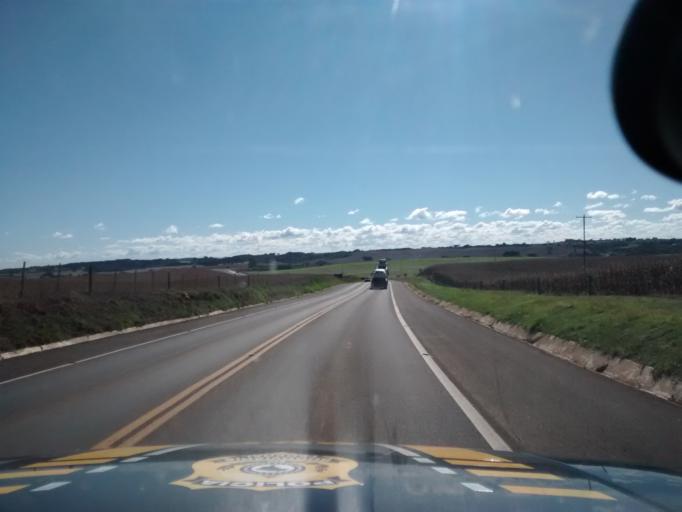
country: BR
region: Rio Grande do Sul
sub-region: Vacaria
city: Vacaria
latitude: -28.3758
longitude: -51.0818
